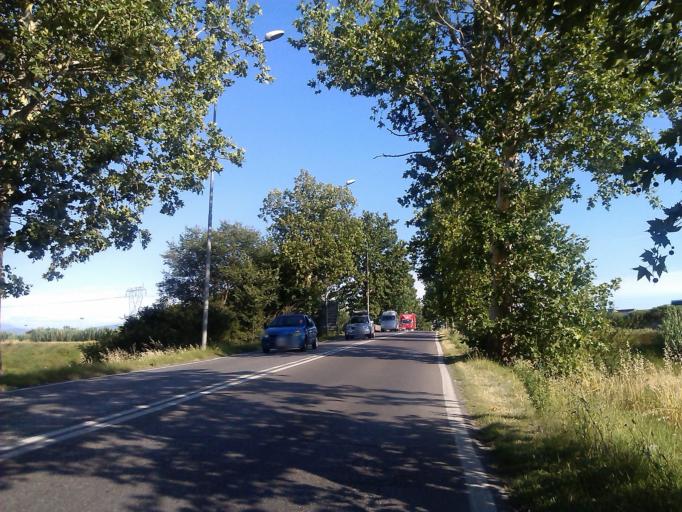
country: IT
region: Tuscany
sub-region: Province of Florence
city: San Donnino
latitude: 43.8141
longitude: 11.1554
